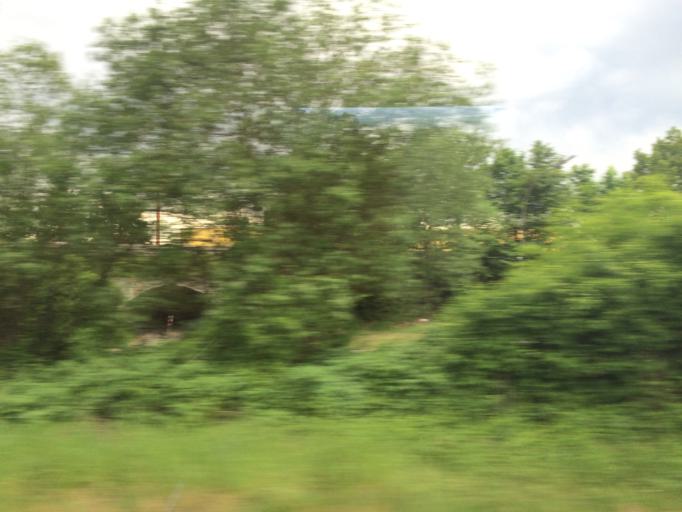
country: DE
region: Bavaria
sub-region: Regierungsbezirk Unterfranken
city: Mainaschaff
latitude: 49.9880
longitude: 9.0872
